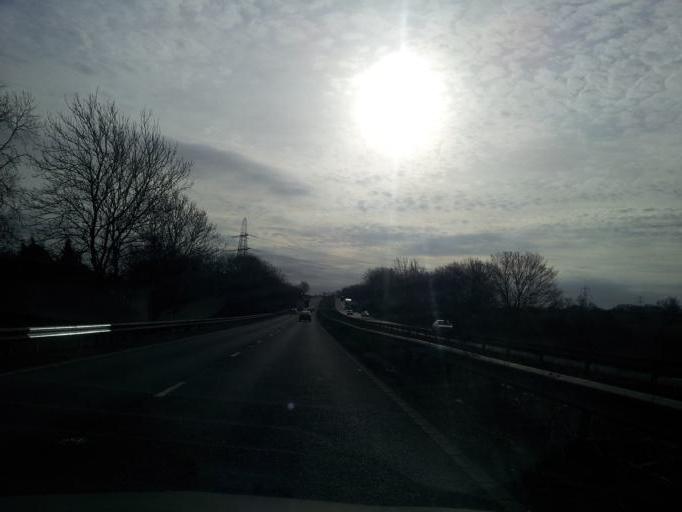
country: GB
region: England
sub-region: Peterborough
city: Upton
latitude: 52.5640
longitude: -0.3816
